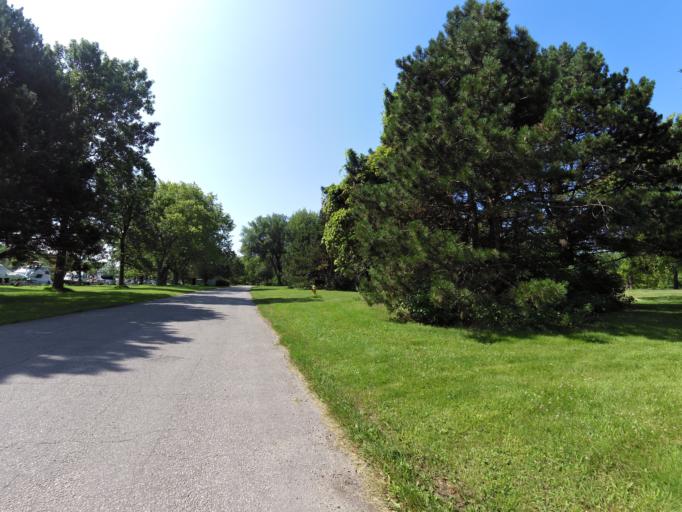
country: CA
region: Ontario
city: Toronto
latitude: 43.6213
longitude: -79.3905
